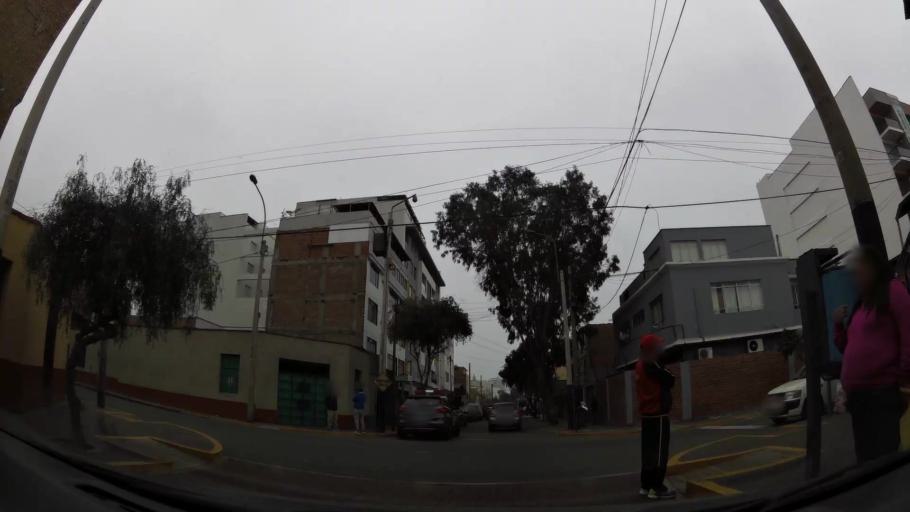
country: PE
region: Lima
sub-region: Lima
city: San Isidro
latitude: -12.1146
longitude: -77.0456
